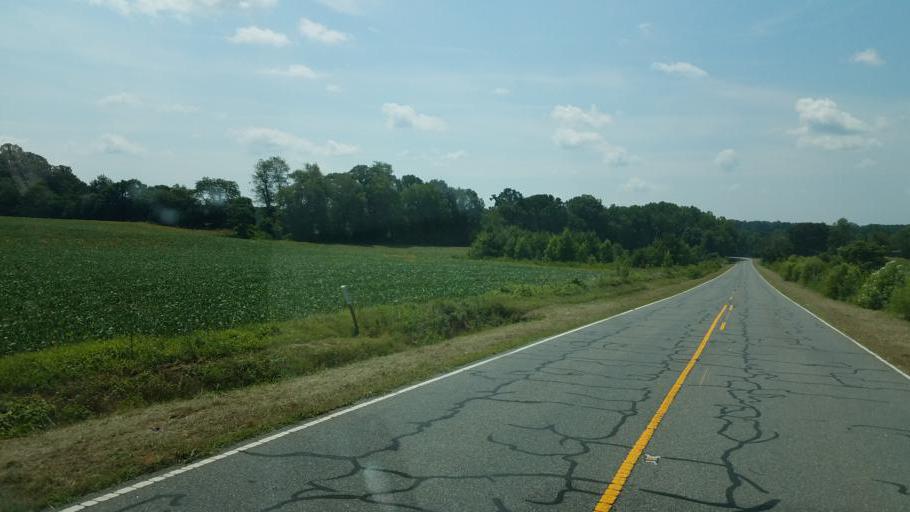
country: US
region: North Carolina
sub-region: Gaston County
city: Cherryville
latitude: 35.4249
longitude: -81.4119
